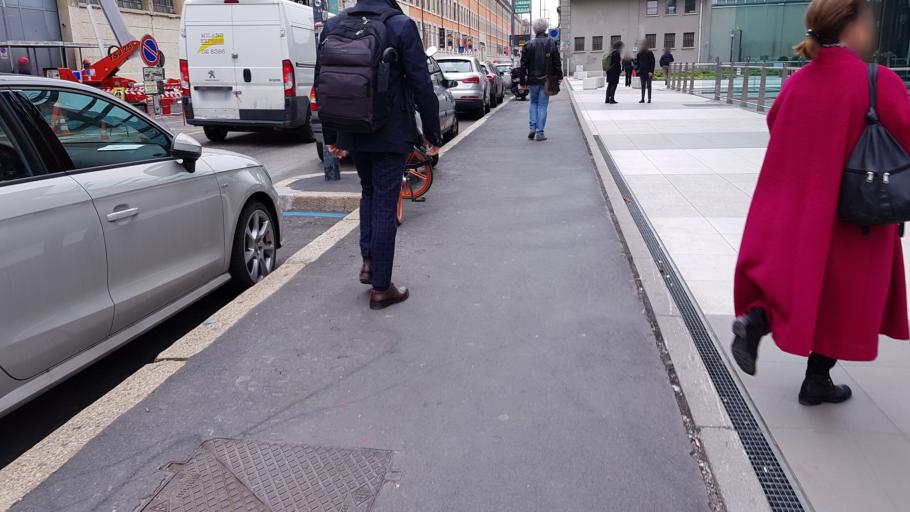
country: IT
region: Lombardy
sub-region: Citta metropolitana di Milano
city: Milano
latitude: 45.4511
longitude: 9.1609
